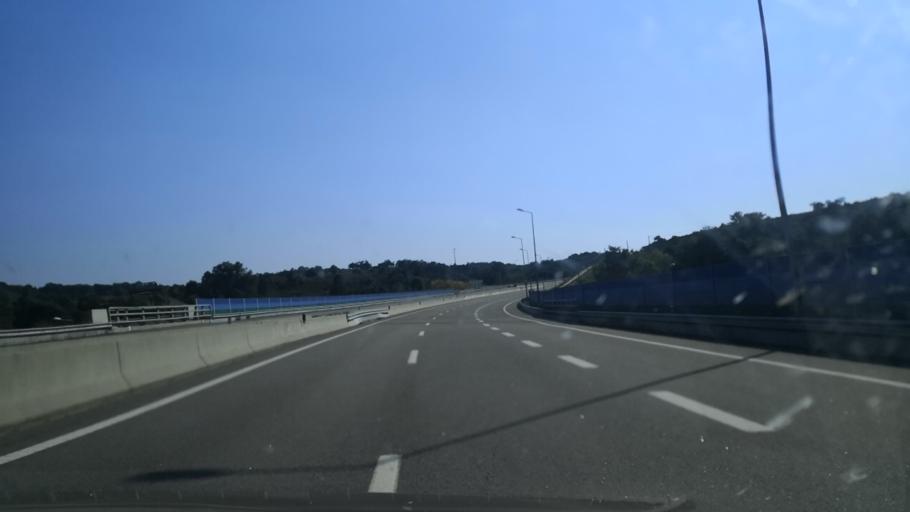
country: PT
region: Braganca
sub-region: Macedo de Cavaleiros
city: Macedo de Cavaleiros
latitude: 41.5791
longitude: -6.9456
